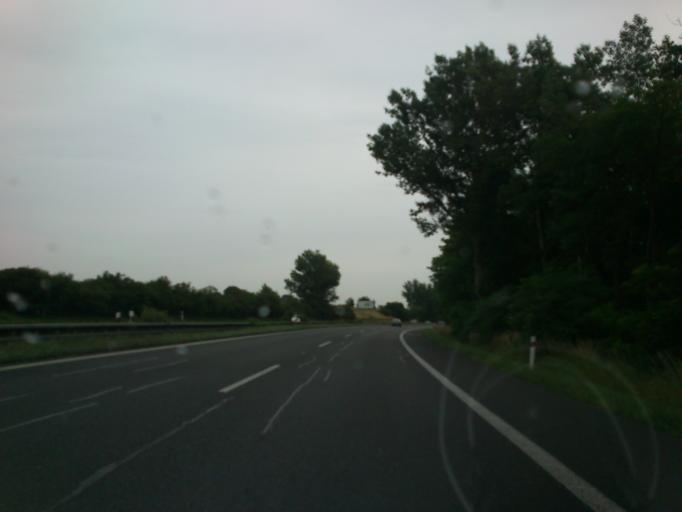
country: CZ
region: Central Bohemia
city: Benatky nad Jizerou
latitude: 50.2606
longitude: 14.7785
